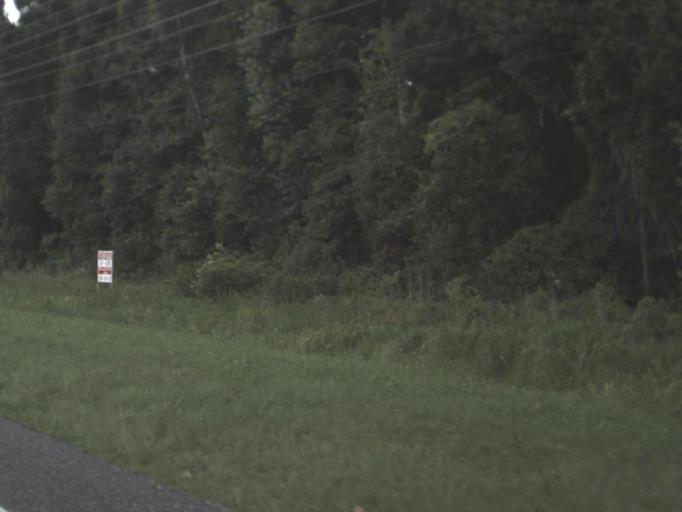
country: US
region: Florida
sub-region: Putnam County
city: Palatka
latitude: 29.7245
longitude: -81.6531
